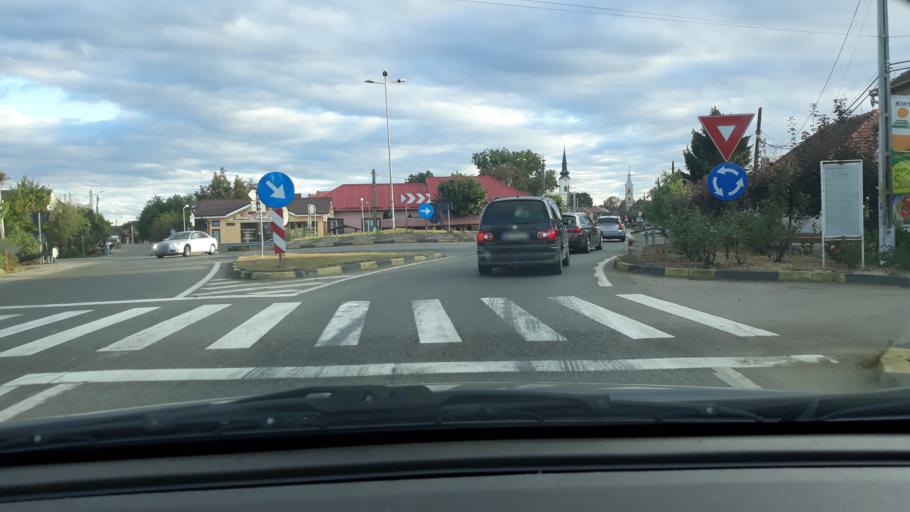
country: RO
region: Bihor
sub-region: Comuna Biharea
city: Biharea
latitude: 47.1574
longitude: 21.9222
